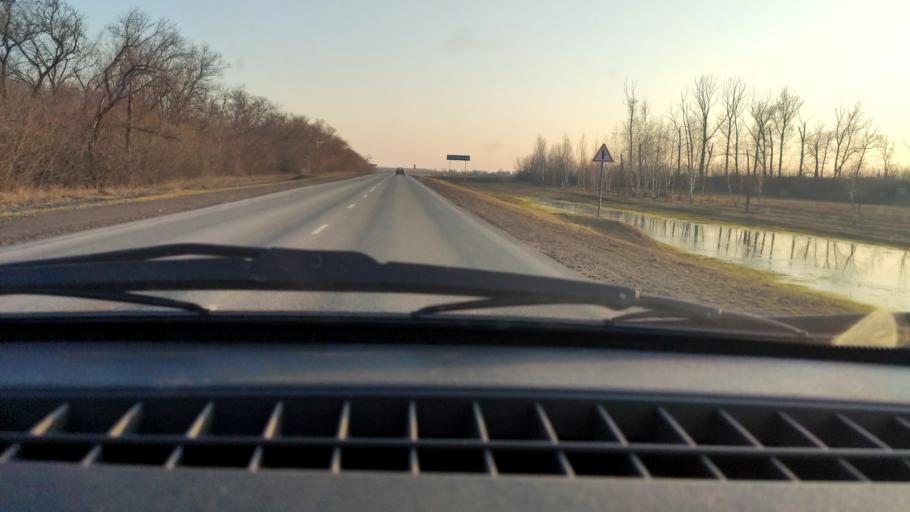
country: RU
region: Bashkortostan
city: Davlekanovo
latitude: 54.2891
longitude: 55.1180
